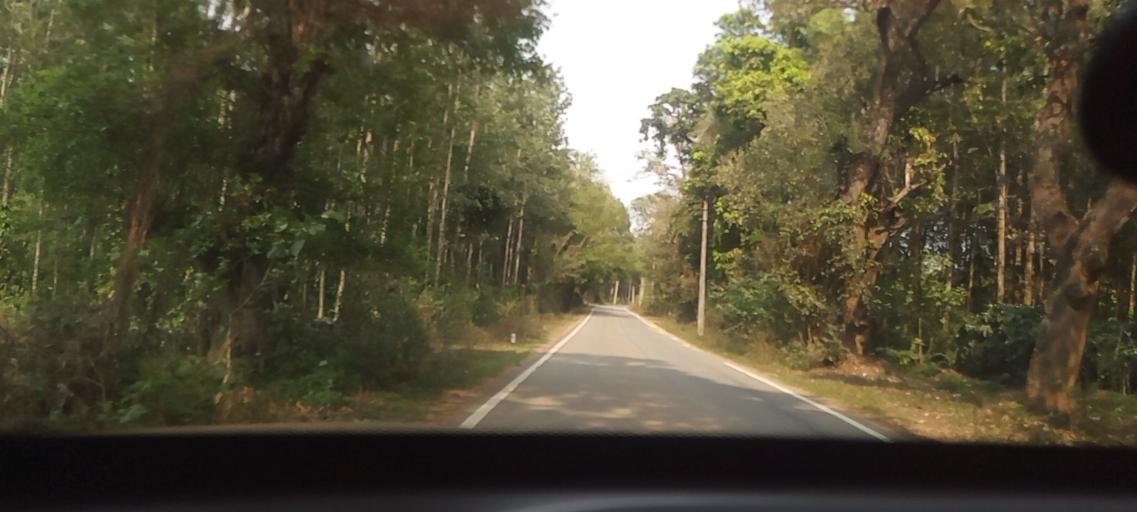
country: IN
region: Karnataka
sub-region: Hassan
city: Belur
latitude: 13.1878
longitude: 75.7870
